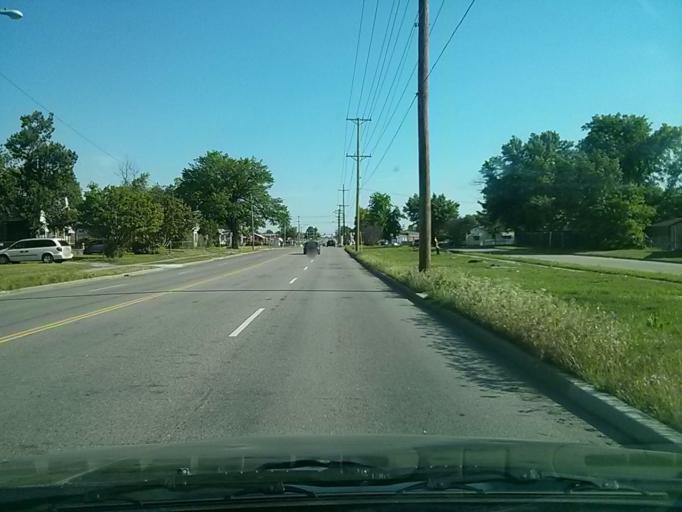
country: US
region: Oklahoma
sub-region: Tulsa County
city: Tulsa
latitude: 36.1887
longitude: -95.9934
